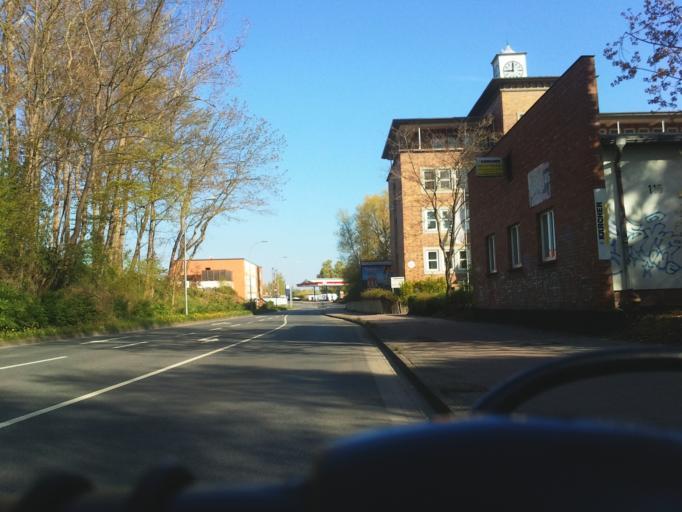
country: DE
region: Mecklenburg-Vorpommern
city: Warnemuende
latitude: 54.1130
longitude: 12.0811
